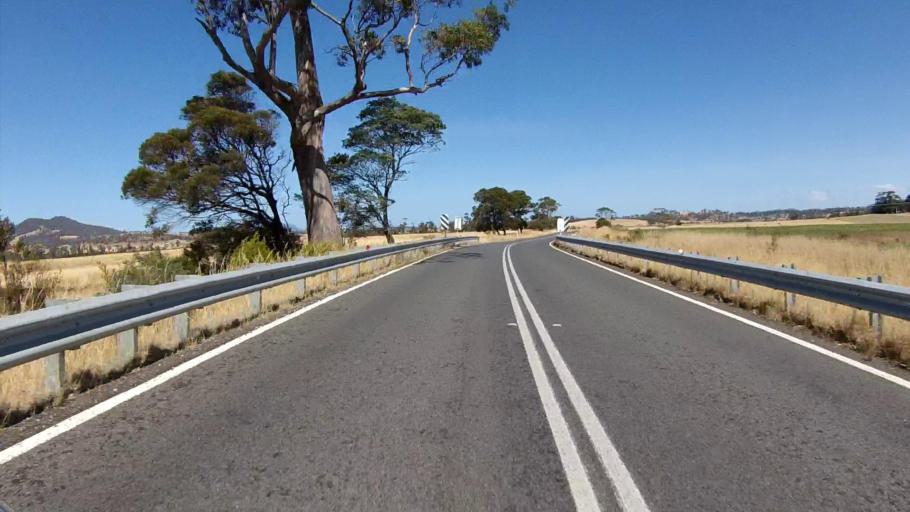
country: AU
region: Tasmania
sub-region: Sorell
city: Sorell
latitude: -42.4460
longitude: 147.9288
